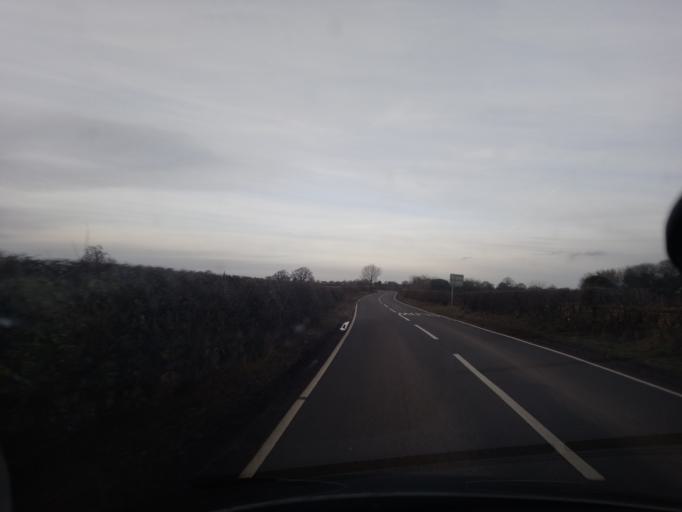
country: GB
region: England
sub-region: Shropshire
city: Prees
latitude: 52.9286
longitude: -2.6799
